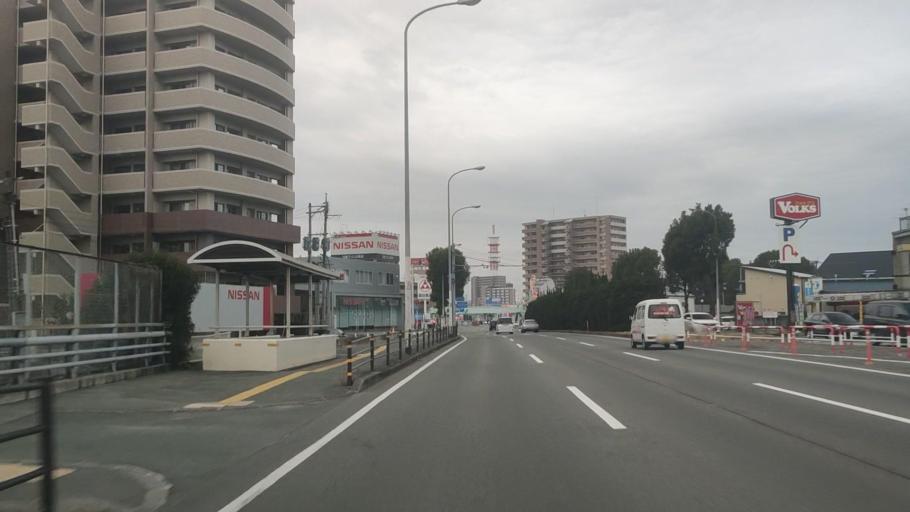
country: JP
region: Kumamoto
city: Kumamoto
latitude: 32.8140
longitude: 130.7501
